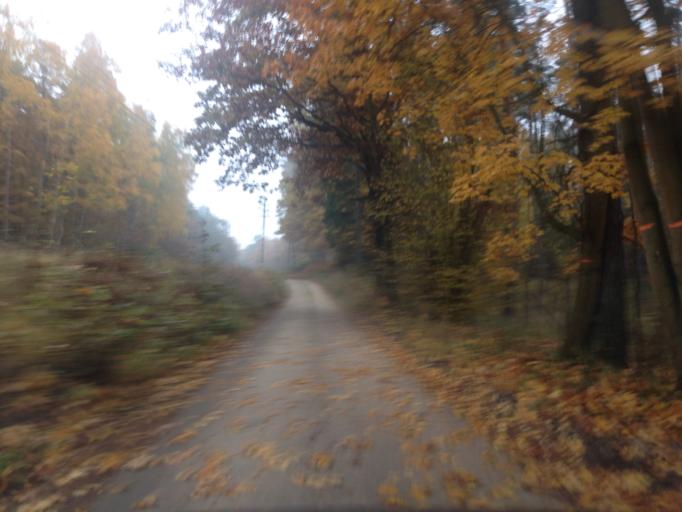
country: PL
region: Kujawsko-Pomorskie
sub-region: Powiat brodnicki
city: Gorzno
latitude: 53.2411
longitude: 19.6817
